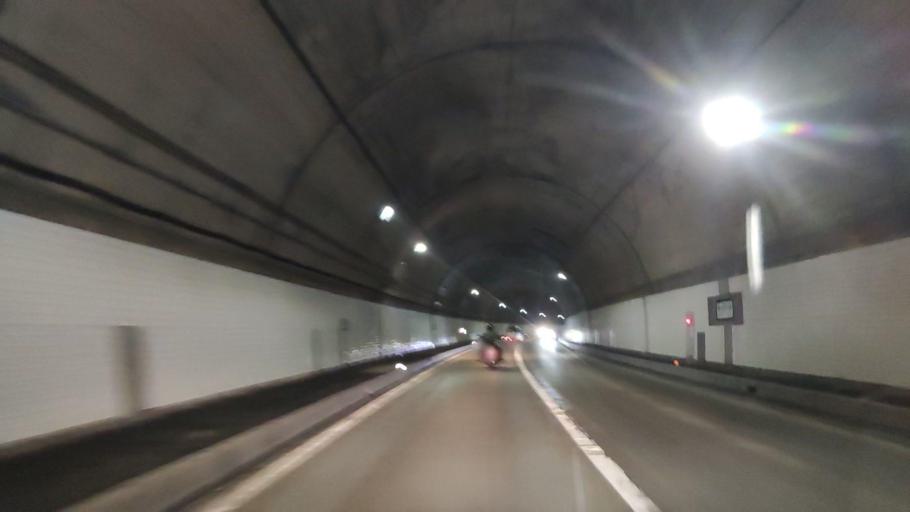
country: JP
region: Akita
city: Yuzawa
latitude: 39.0084
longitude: 140.3721
